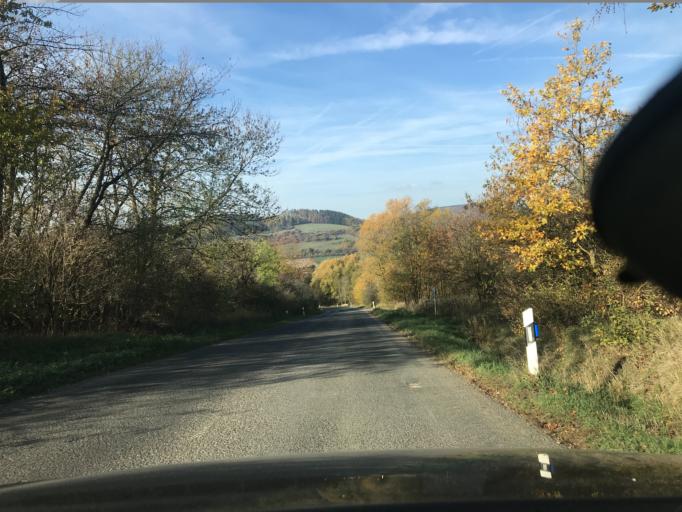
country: DE
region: Hesse
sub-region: Regierungsbezirk Kassel
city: Grossalmerode
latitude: 51.2112
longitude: 9.8063
